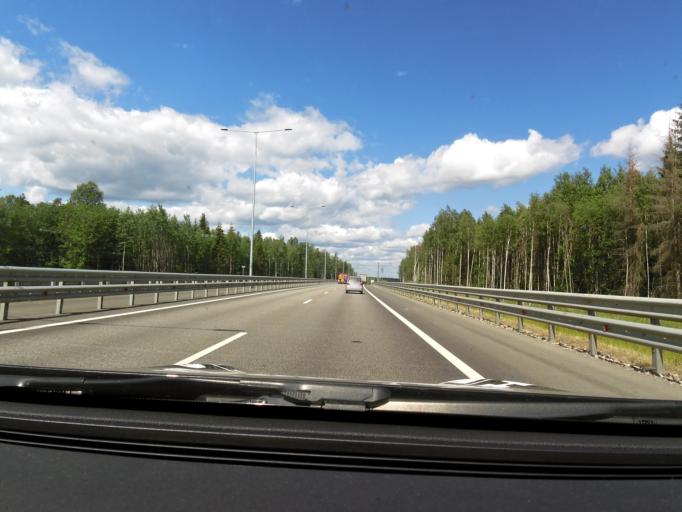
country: RU
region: Tverskaya
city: Vyshniy Volochek
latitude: 57.3847
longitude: 34.5601
